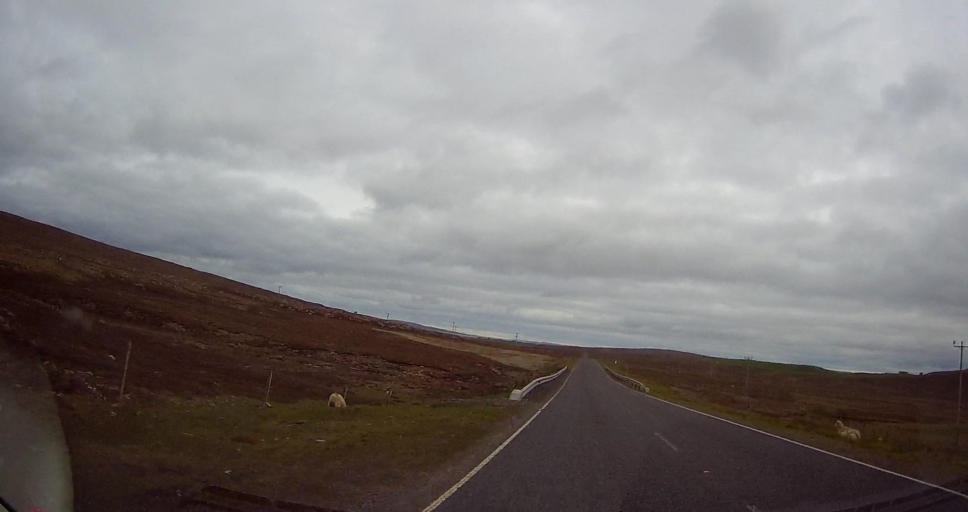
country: GB
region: Scotland
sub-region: Shetland Islands
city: Shetland
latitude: 60.7228
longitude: -0.9087
